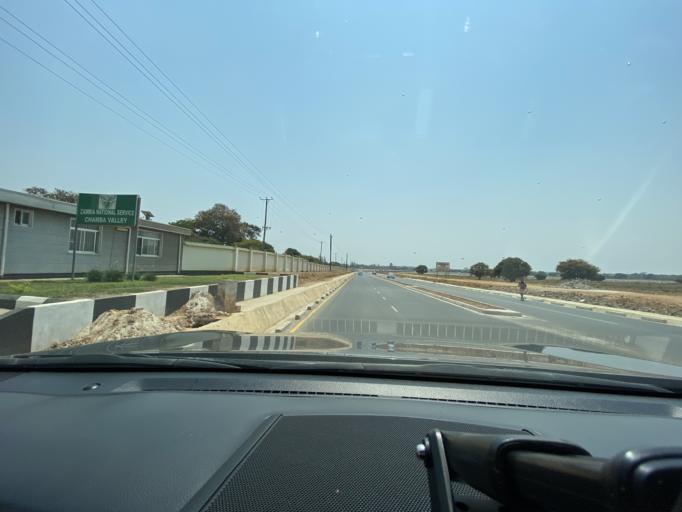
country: ZM
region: Lusaka
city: Lusaka
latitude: -15.3629
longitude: 28.3481
